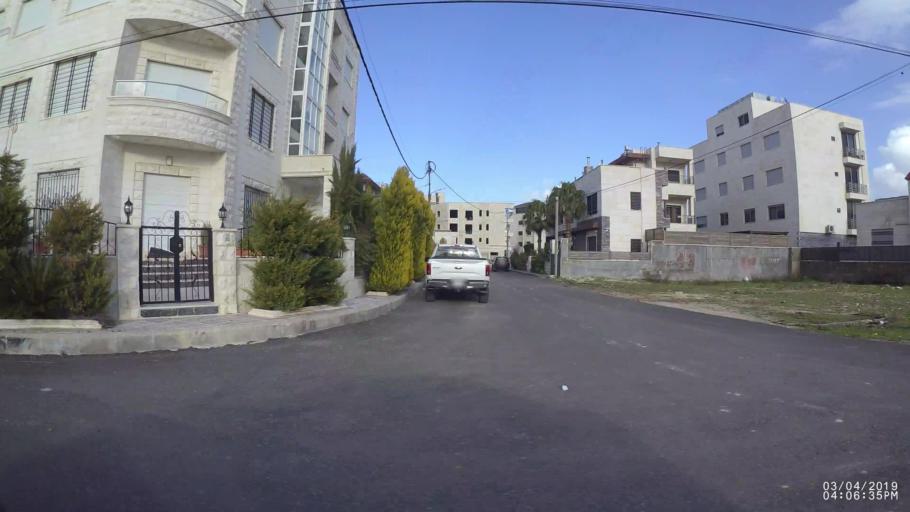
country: JO
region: Amman
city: Al Bunayyat ash Shamaliyah
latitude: 31.9103
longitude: 35.8791
